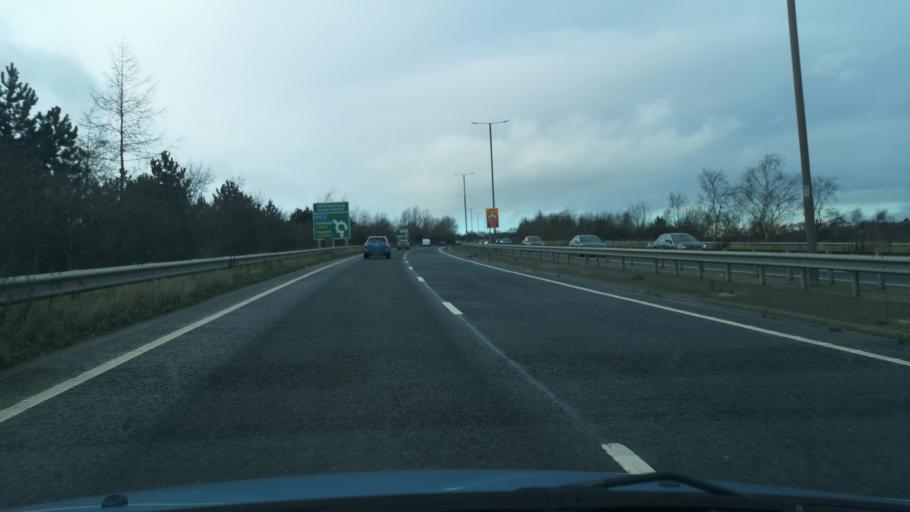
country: GB
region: England
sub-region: Barnsley
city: Wombwell
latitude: 53.5118
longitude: -1.4060
